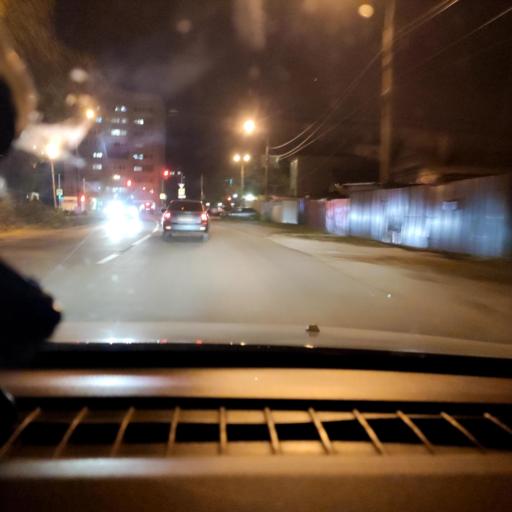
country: RU
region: Samara
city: Samara
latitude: 53.1983
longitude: 50.1986
